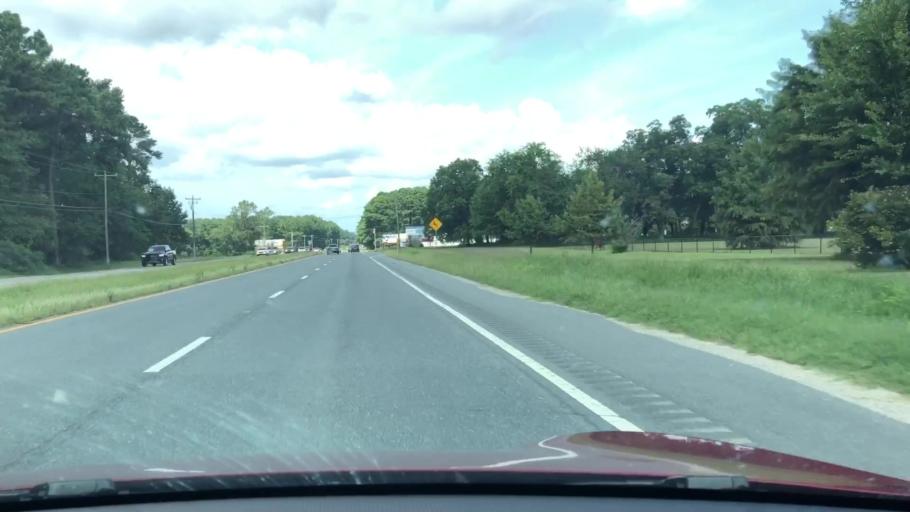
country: US
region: Virginia
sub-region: Northampton County
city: Cape Charles
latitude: 37.2512
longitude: -75.9726
